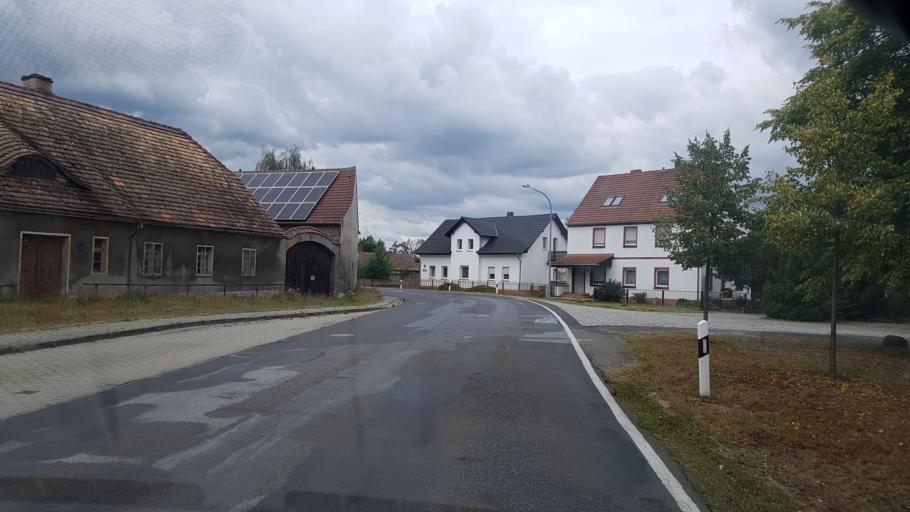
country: DE
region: Saxony
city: Klitten
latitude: 51.3845
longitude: 14.6620
